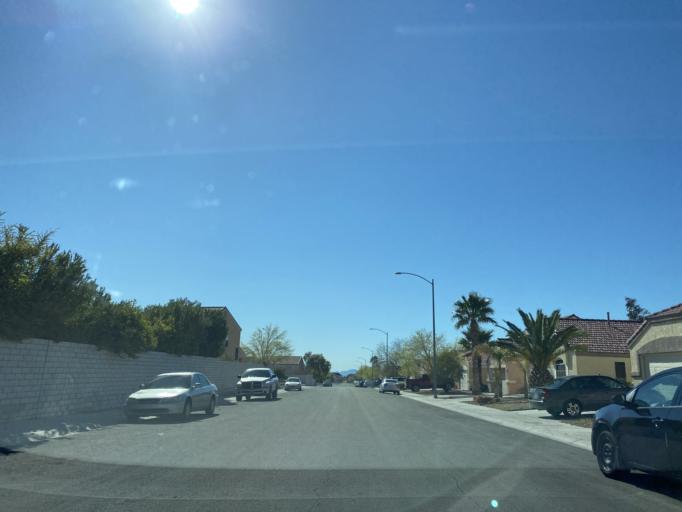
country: US
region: Nevada
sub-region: Clark County
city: Summerlin South
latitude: 36.3058
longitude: -115.2910
